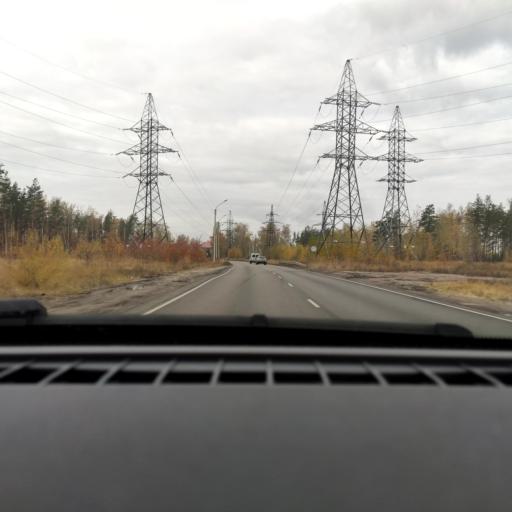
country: RU
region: Voronezj
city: Somovo
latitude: 51.7277
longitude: 39.3015
